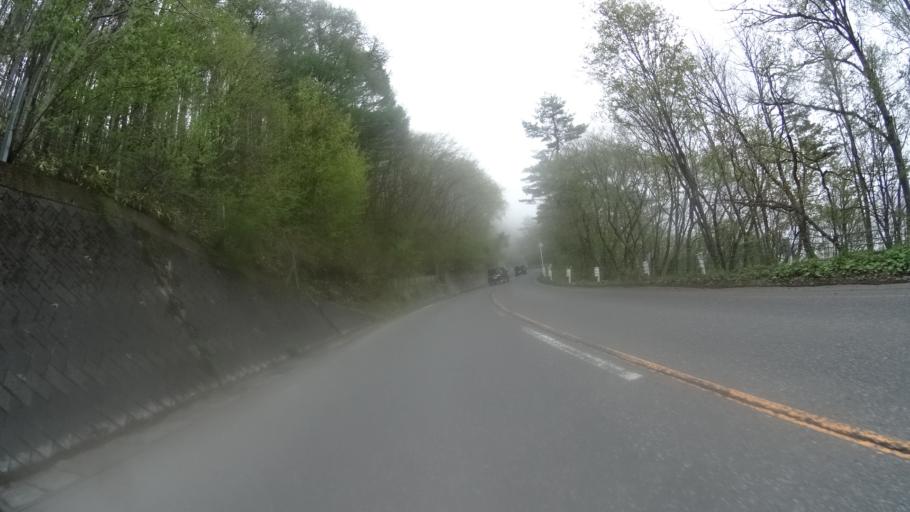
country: JP
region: Nagano
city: Nakano
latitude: 36.7240
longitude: 138.4672
